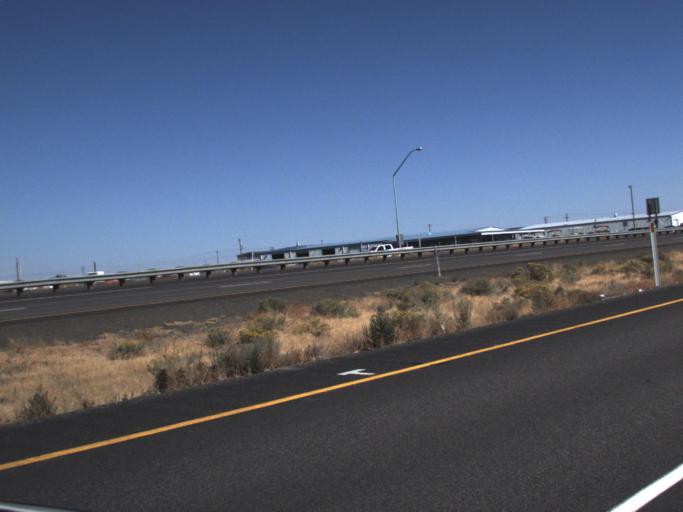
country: US
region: Washington
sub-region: Franklin County
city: Pasco
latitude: 46.2516
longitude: -119.0802
